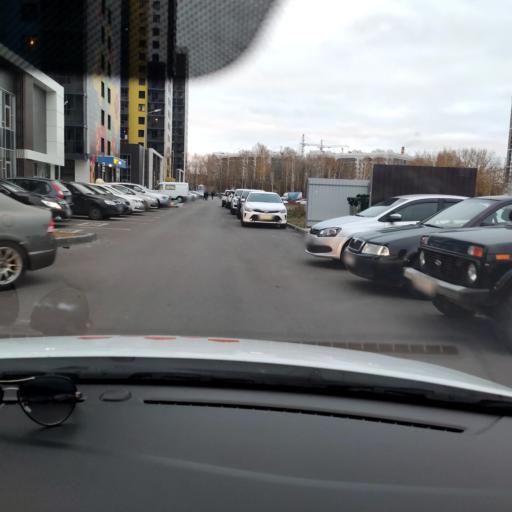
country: RU
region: Tatarstan
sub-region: Gorod Kazan'
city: Kazan
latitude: 55.7623
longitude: 49.1927
